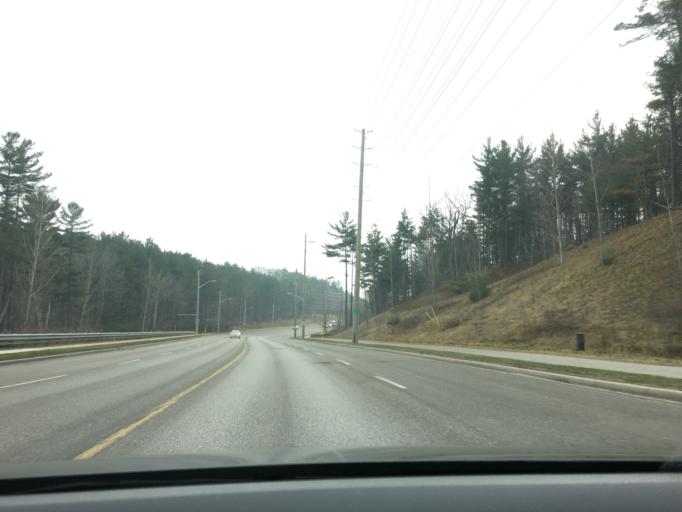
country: CA
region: Ontario
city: Barrie
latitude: 44.3889
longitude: -79.7319
